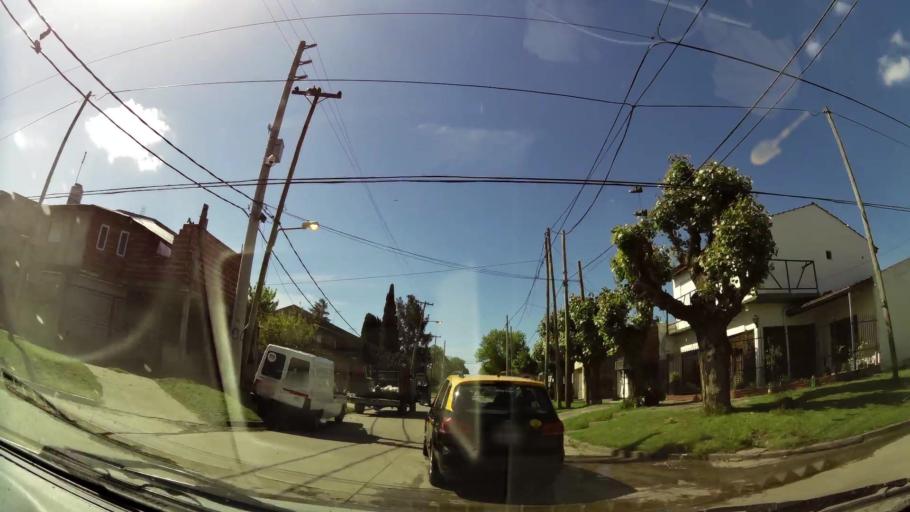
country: AR
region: Buenos Aires
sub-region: Partido de Quilmes
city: Quilmes
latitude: -34.8013
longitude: -58.2699
